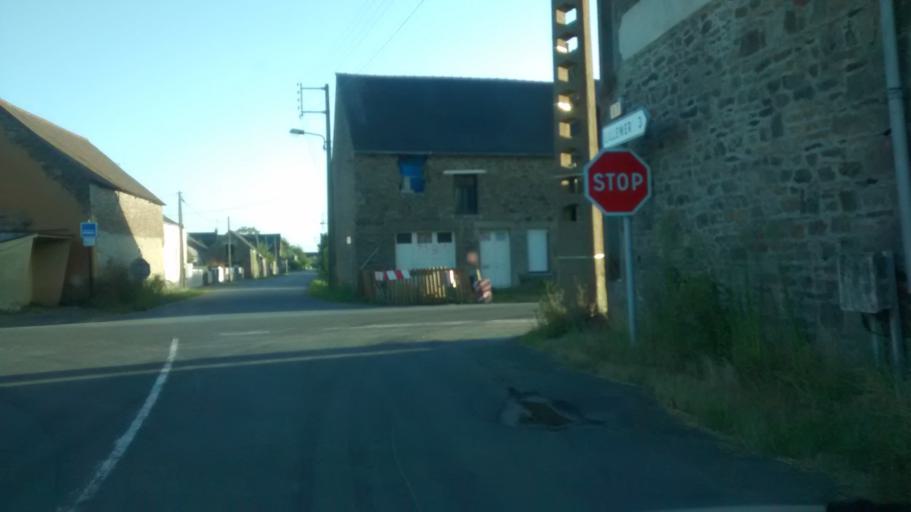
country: FR
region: Brittany
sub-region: Departement d'Ille-et-Vilaine
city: La Fresnais
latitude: 48.5901
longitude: -1.8584
